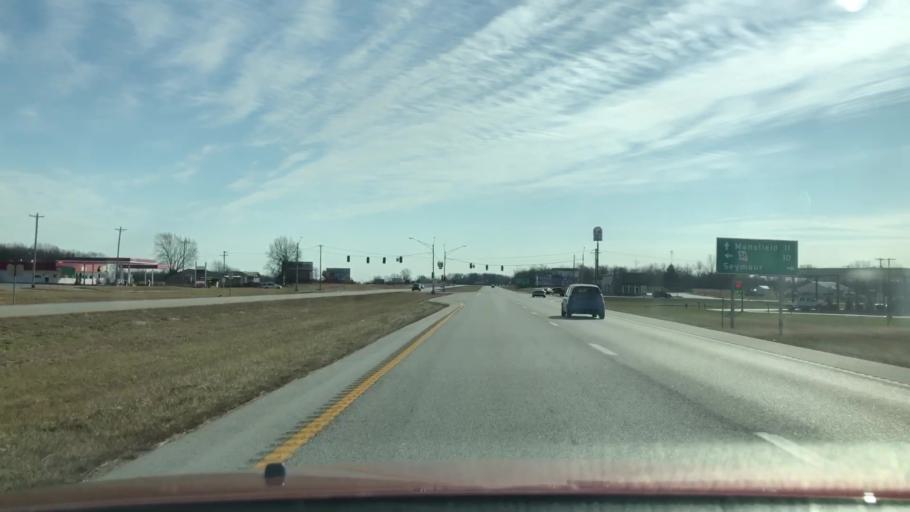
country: US
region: Missouri
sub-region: Webster County
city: Seymour
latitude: 37.1511
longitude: -92.7548
